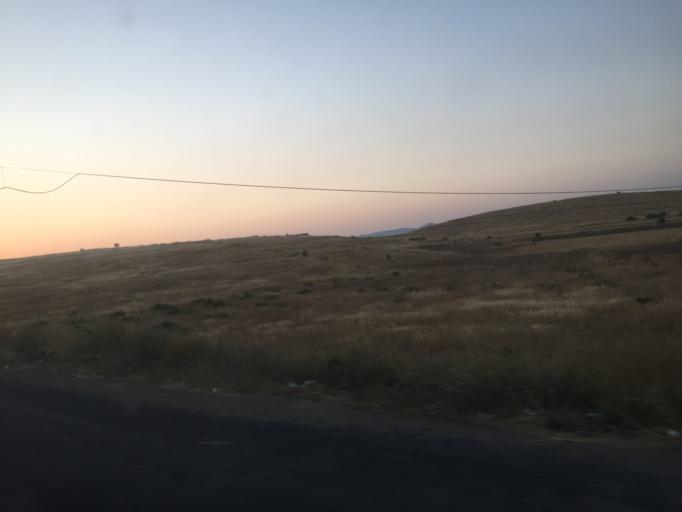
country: TR
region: Mardin
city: Kindirip
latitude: 37.4636
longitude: 41.2263
